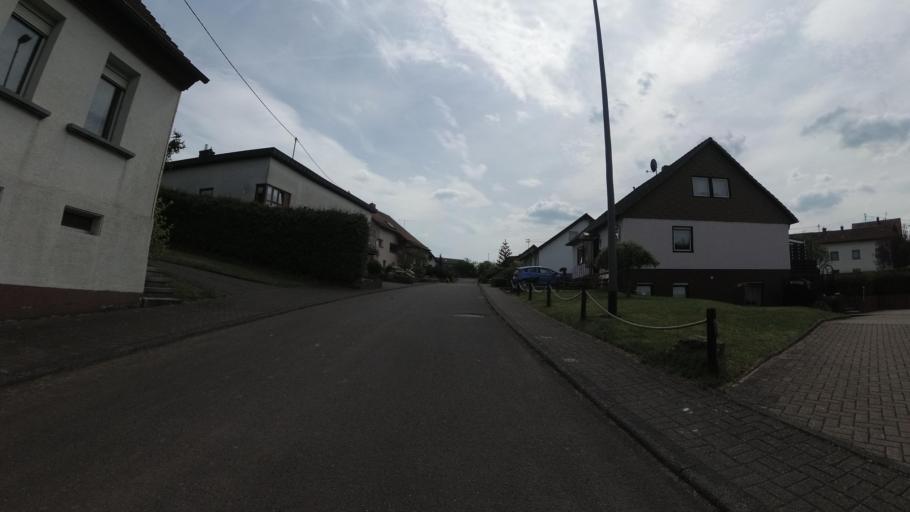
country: DE
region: Rheinland-Pfalz
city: Fohren-Linden
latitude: 49.5851
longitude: 7.2905
